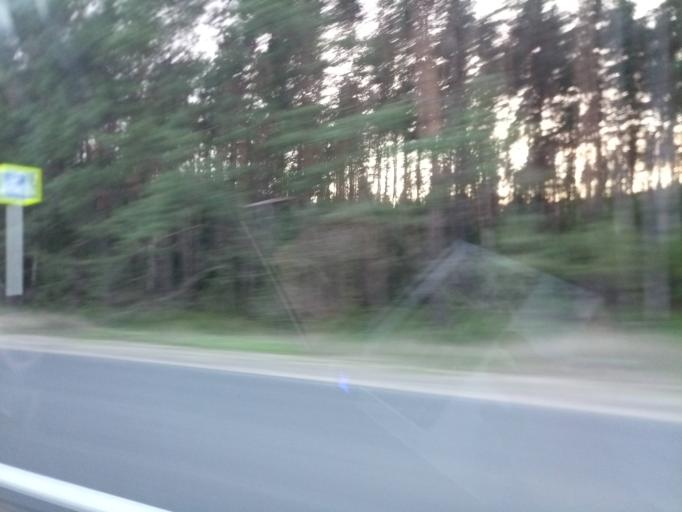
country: RU
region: Moskovskaya
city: Noginsk-9
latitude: 56.1031
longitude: 38.5859
